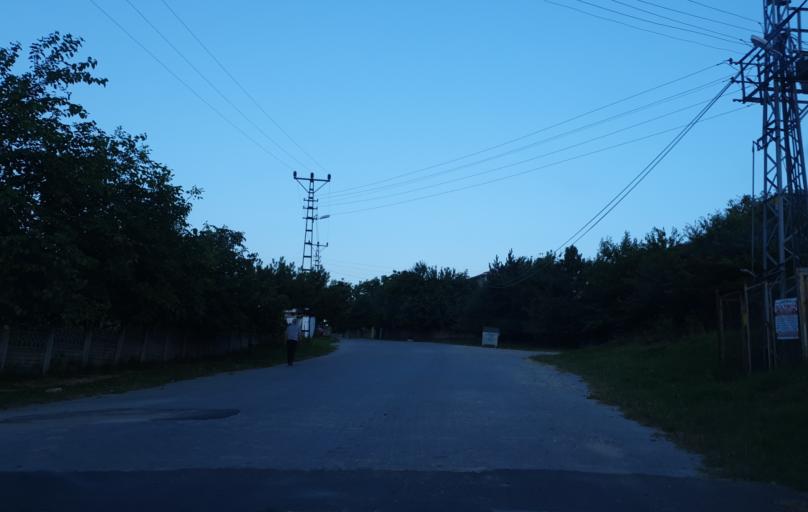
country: TR
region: Tekirdag
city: Velimese
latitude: 41.3496
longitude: 27.8812
